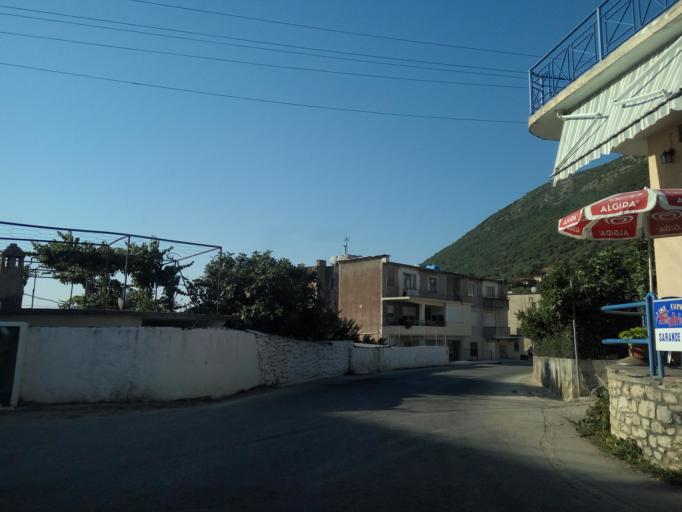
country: AL
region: Vlore
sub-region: Rrethi i Sarandes
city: Lukove
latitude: 39.9593
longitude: 19.9622
